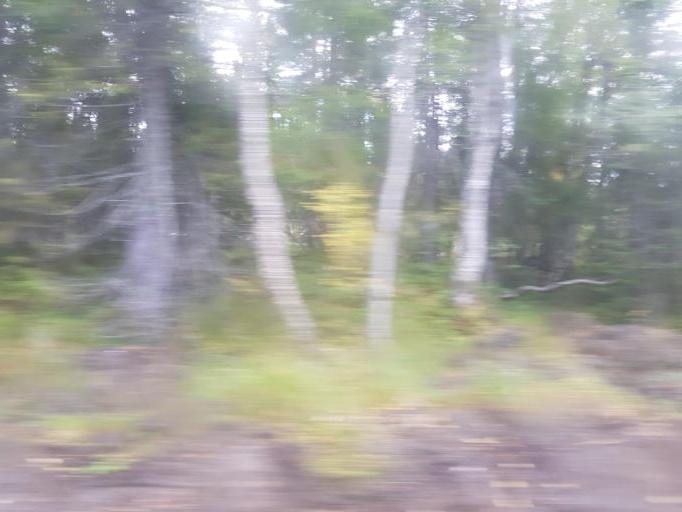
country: NO
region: Sor-Trondelag
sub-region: Trondheim
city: Trondheim
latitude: 63.4167
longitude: 10.2889
